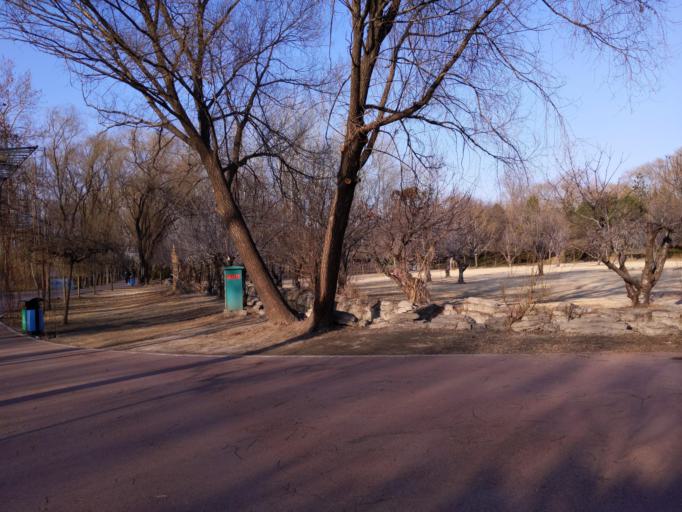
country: CN
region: Henan Sheng
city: Puyang
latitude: 35.7771
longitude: 114.9600
